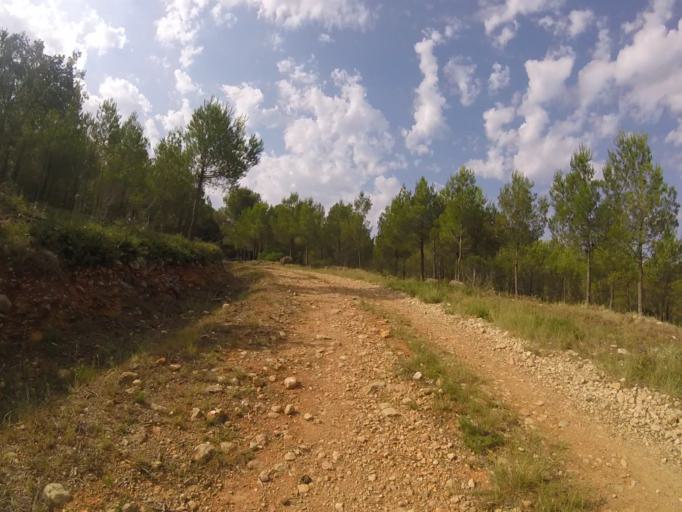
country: ES
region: Valencia
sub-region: Provincia de Castello
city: Alcala de Xivert
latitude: 40.3639
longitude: 0.2028
